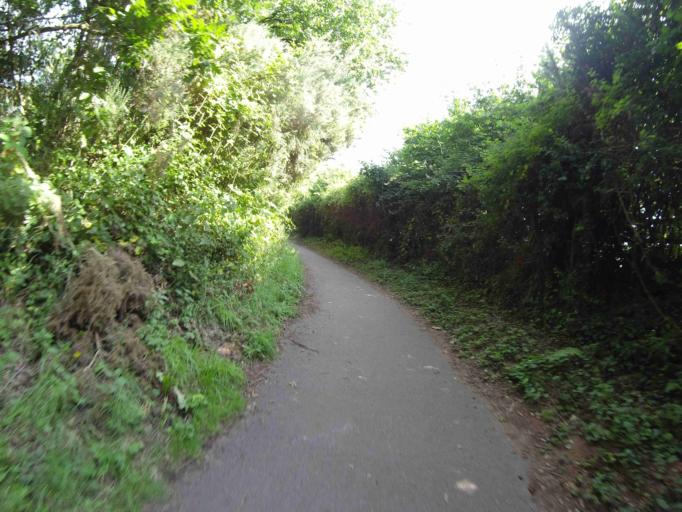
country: GB
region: England
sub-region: Devon
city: Budleigh Salterton
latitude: 50.6395
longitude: -3.3441
